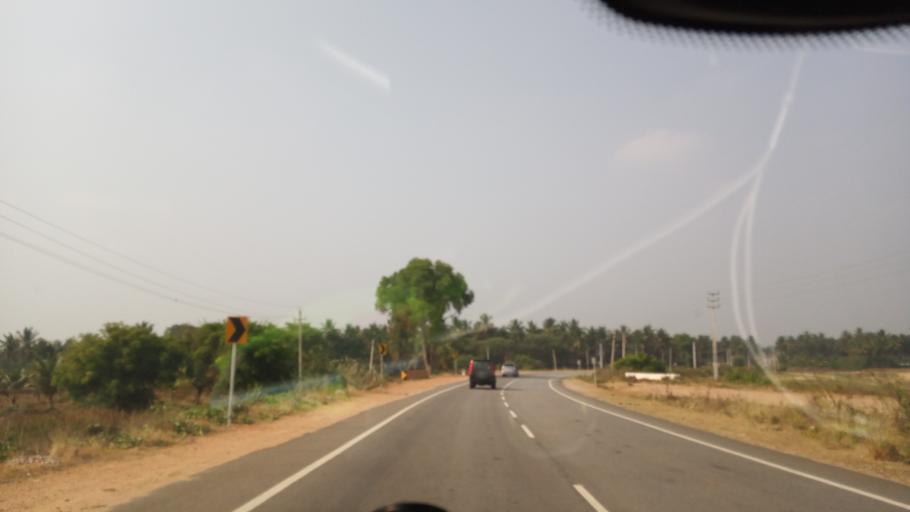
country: IN
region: Karnataka
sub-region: Mandya
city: Nagamangala
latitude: 12.7424
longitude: 76.7256
